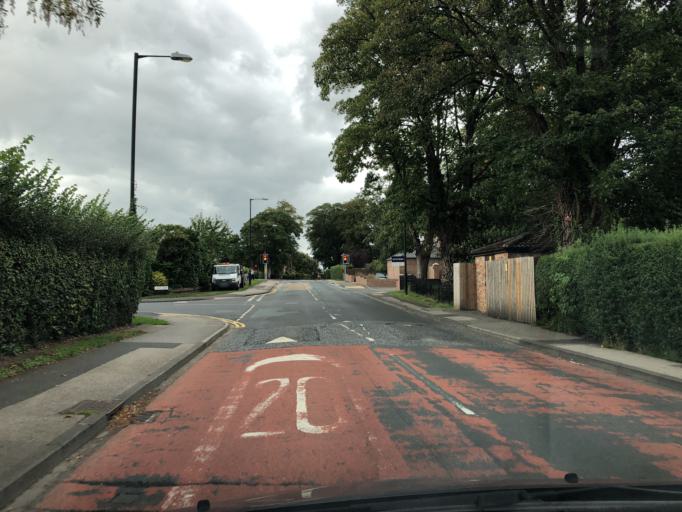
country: GB
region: England
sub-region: North Yorkshire
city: Ripon
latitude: 54.1260
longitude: -1.5266
